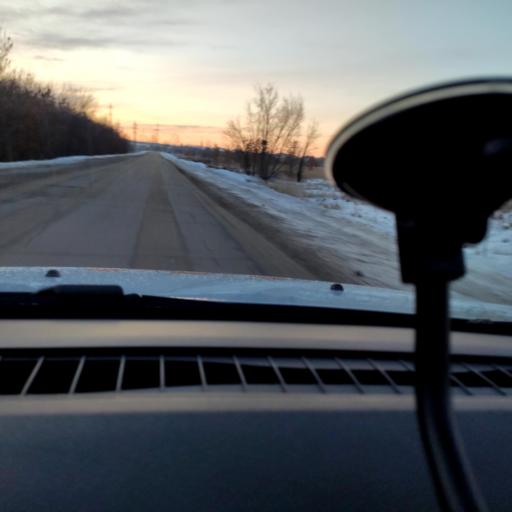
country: RU
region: Samara
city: Dubovyy Umet
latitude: 53.0899
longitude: 50.2325
